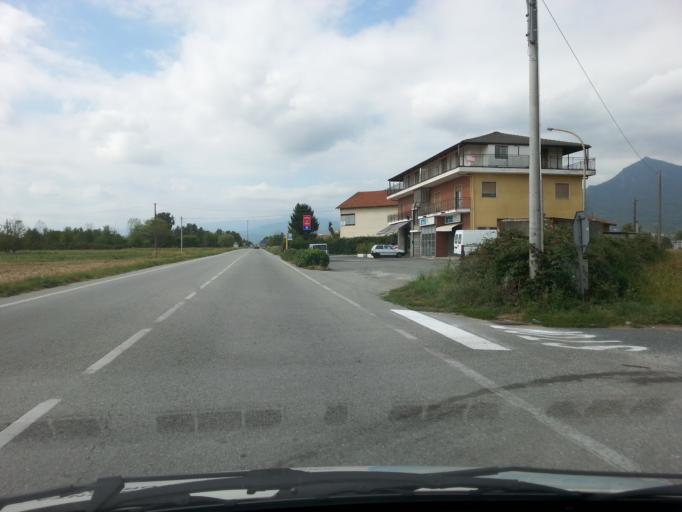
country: IT
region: Piedmont
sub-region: Provincia di Torino
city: Piscina
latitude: 44.9636
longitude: 7.4213
